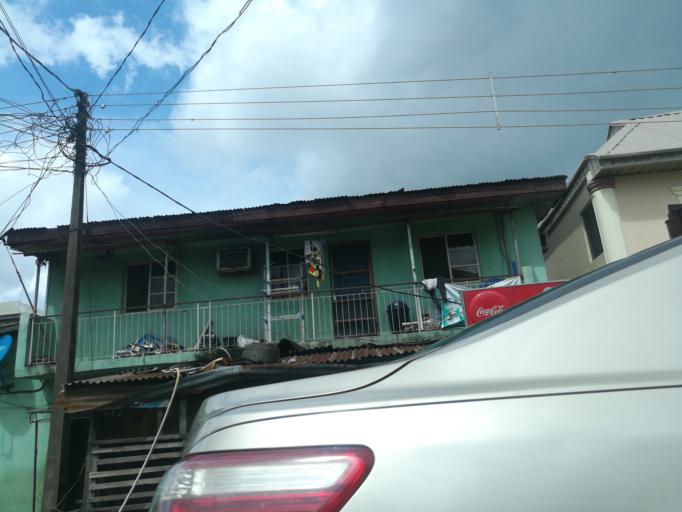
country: NG
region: Lagos
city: Somolu
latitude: 6.5390
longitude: 3.3621
